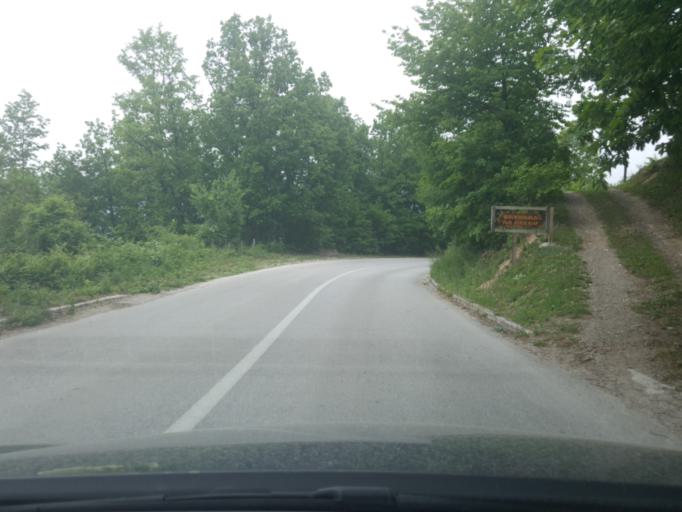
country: RS
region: Central Serbia
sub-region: Zlatiborski Okrug
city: Bajina Basta
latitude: 43.9472
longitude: 19.5551
